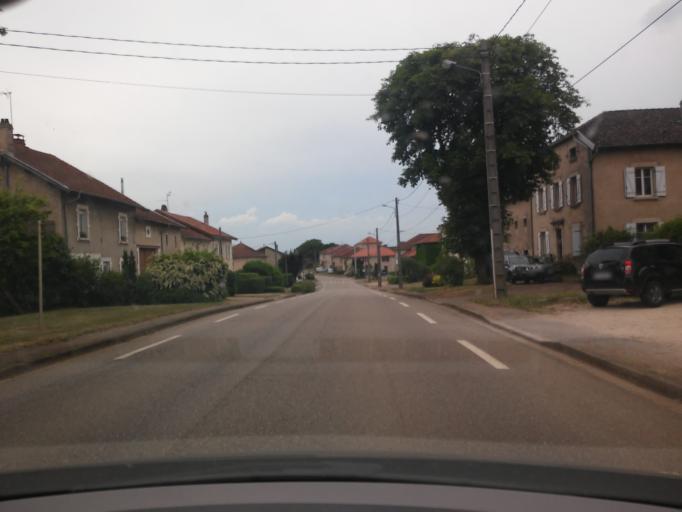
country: FR
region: Lorraine
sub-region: Departement de Meurthe-et-Moselle
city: Montauville
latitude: 48.8873
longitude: 5.8976
